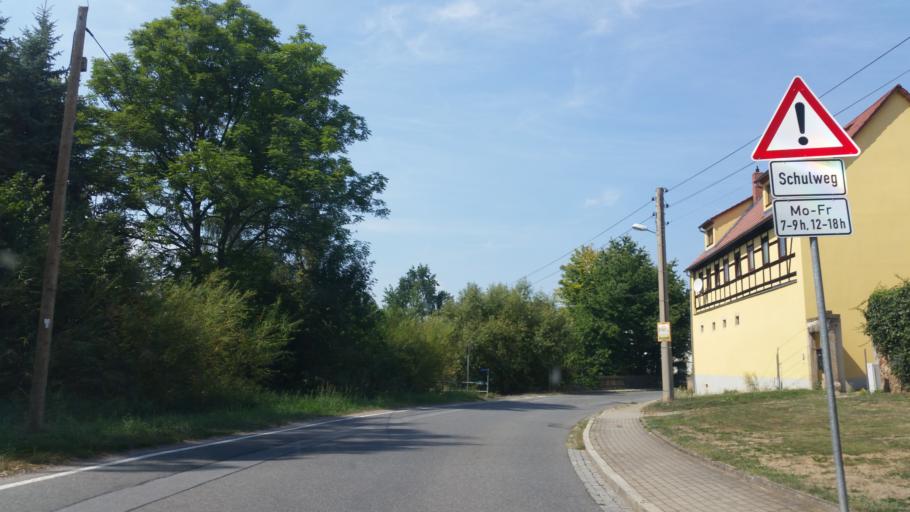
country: DE
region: Saxony
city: Klipphausen
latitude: 51.0689
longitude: 13.5338
